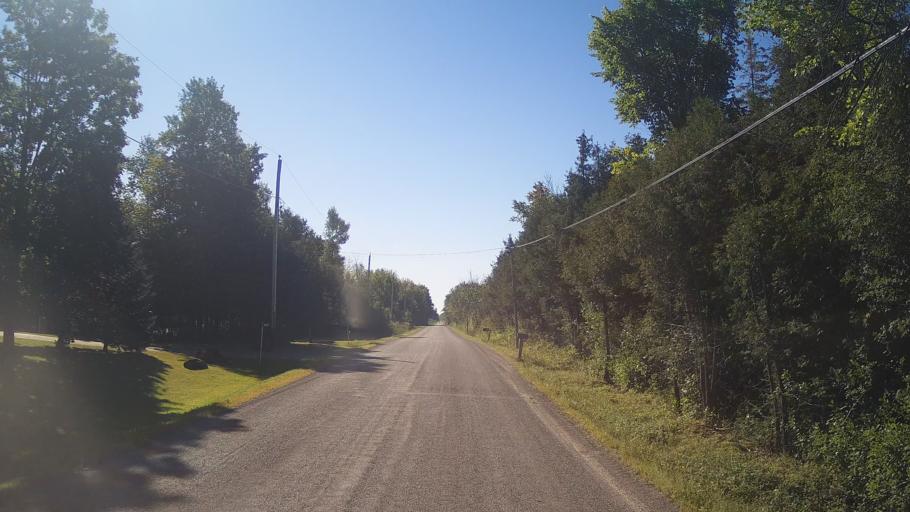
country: CA
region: Ontario
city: Prescott
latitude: 44.9978
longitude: -75.5954
